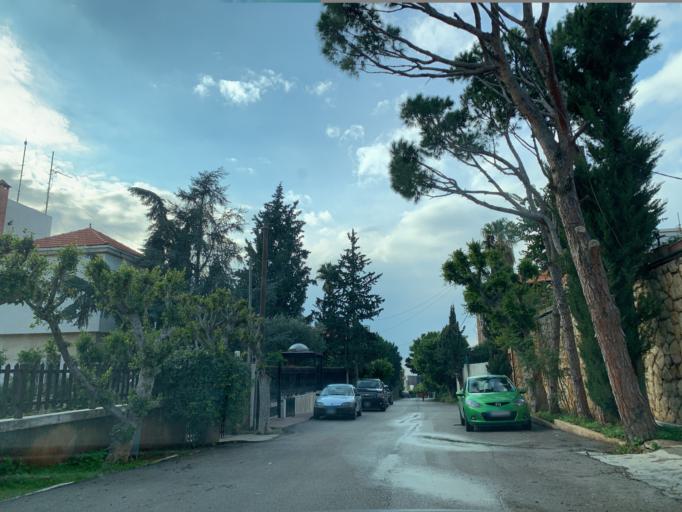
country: LB
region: Mont-Liban
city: Baabda
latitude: 33.8510
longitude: 35.5776
